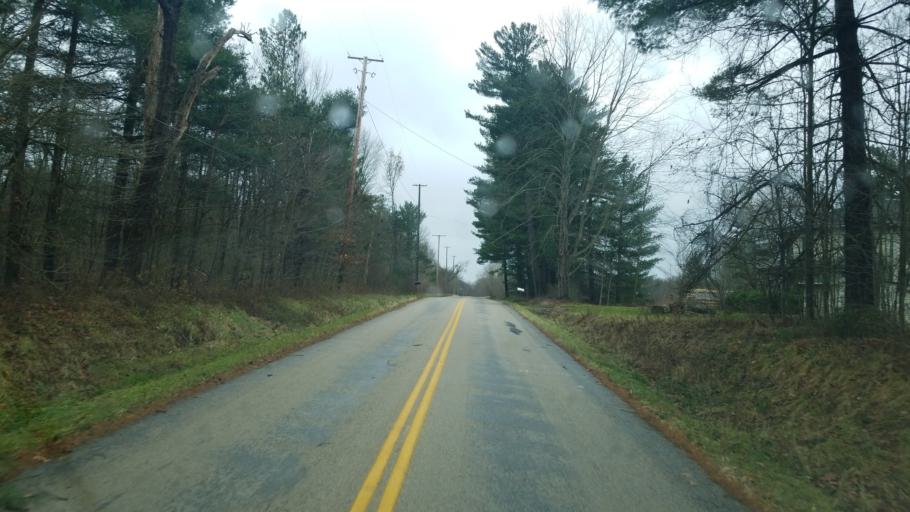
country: US
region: Ohio
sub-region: Ashtabula County
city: Roaming Shores
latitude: 41.7236
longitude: -80.8746
